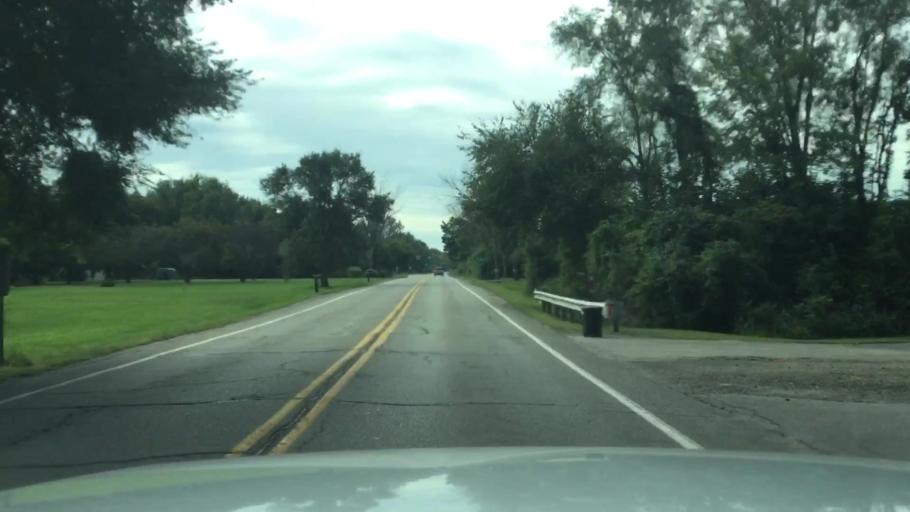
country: US
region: Michigan
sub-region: Wayne County
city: Belleville
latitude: 42.1783
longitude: -83.4830
